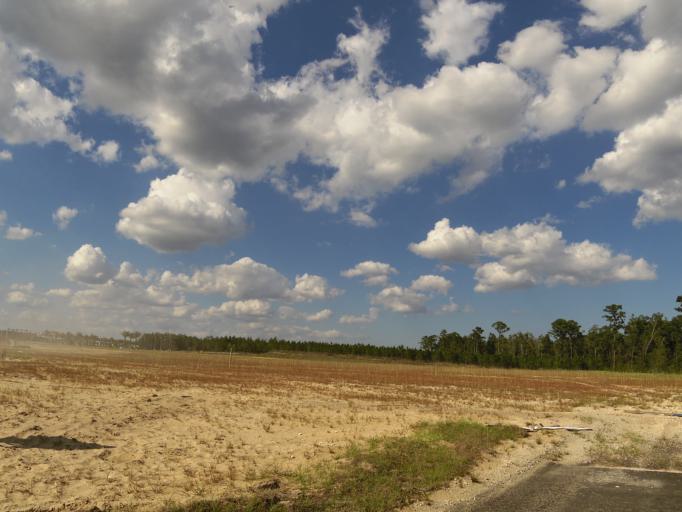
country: US
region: Florida
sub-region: Saint Johns County
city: Palm Valley
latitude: 30.1644
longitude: -81.5051
